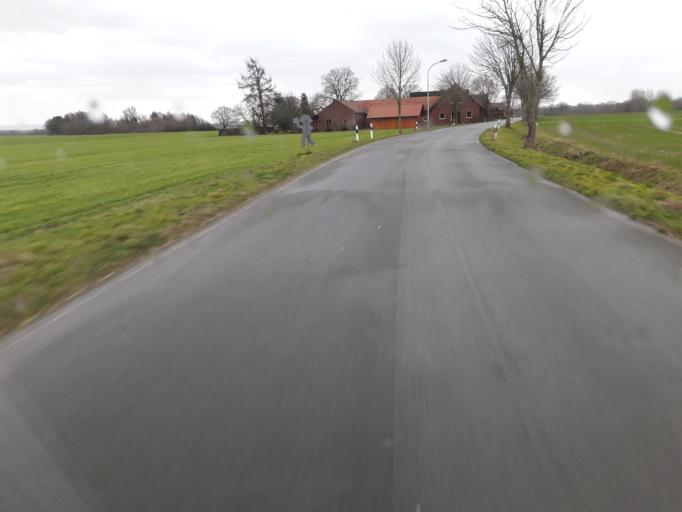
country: DE
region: Lower Saxony
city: Raddestorf
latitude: 52.4462
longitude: 8.9888
